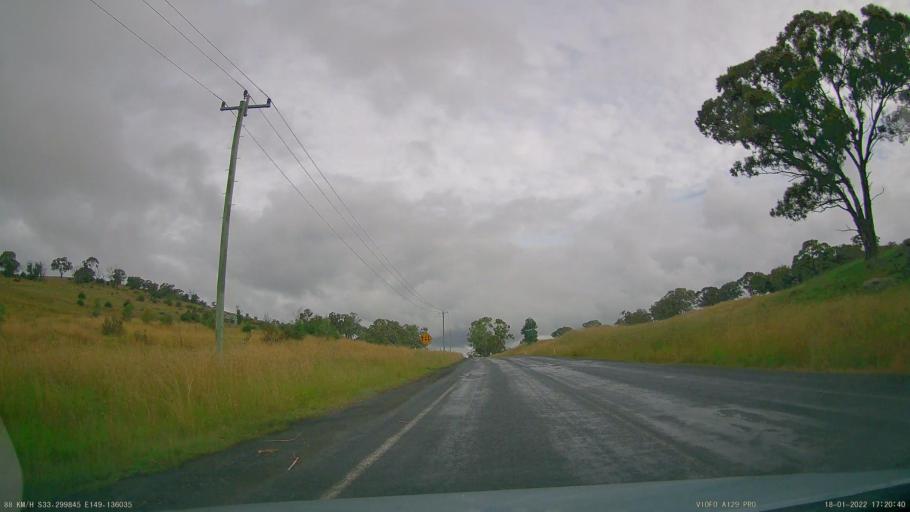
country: AU
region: New South Wales
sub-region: Orange Municipality
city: Orange
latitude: -33.3000
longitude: 149.1361
